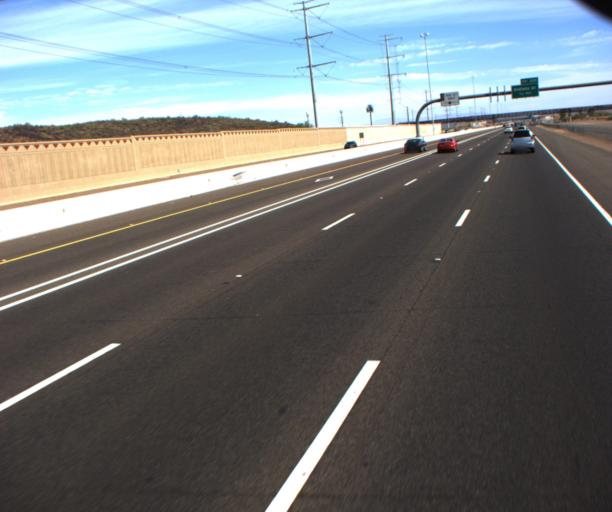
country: US
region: Arizona
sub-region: Maricopa County
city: Anthem
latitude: 33.7429
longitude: -112.1236
